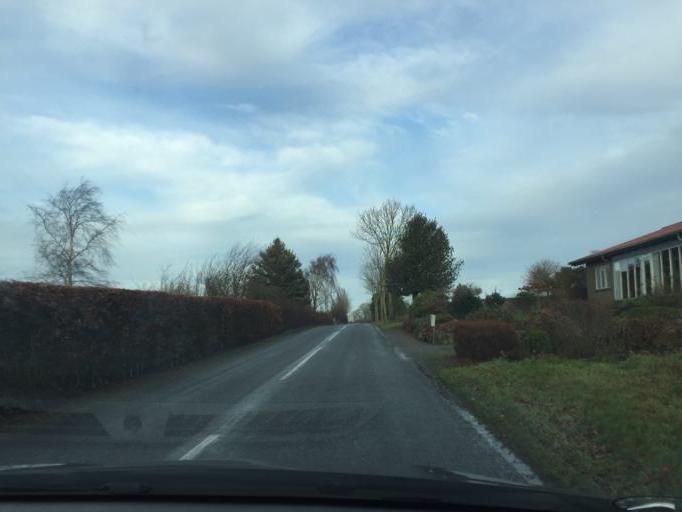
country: DK
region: South Denmark
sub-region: Faaborg-Midtfyn Kommune
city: Ringe
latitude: 55.1760
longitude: 10.4049
